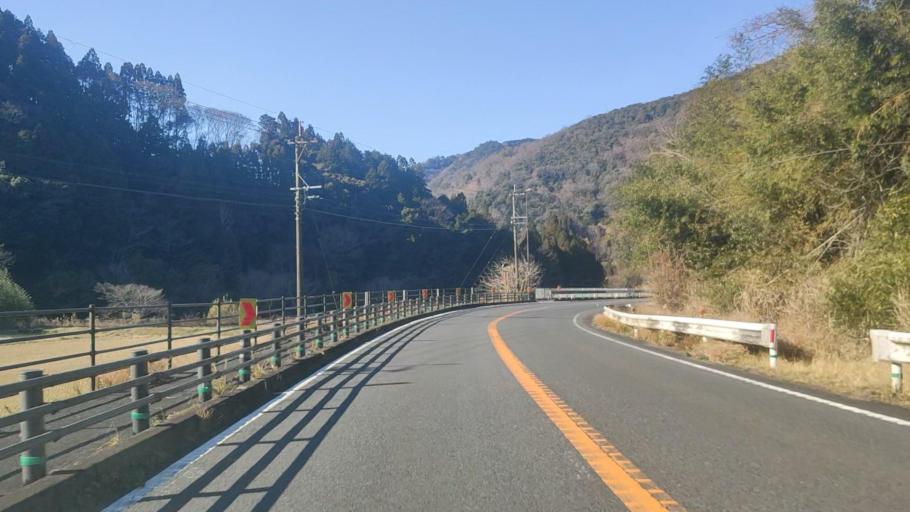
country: JP
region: Oita
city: Usuki
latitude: 33.0038
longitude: 131.7429
